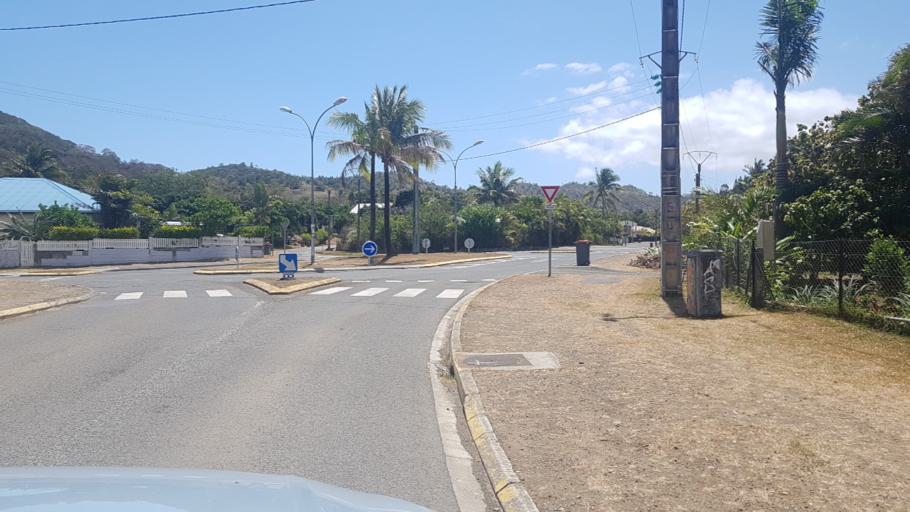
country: NC
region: South Province
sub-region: Dumbea
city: Dumbea
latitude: -22.1374
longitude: 166.4347
